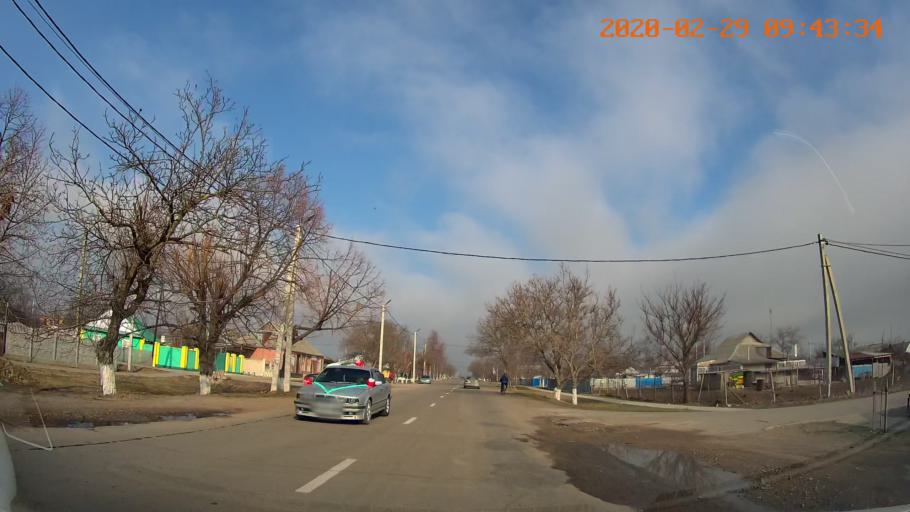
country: MD
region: Telenesti
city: Crasnoe
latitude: 46.6452
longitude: 29.8212
